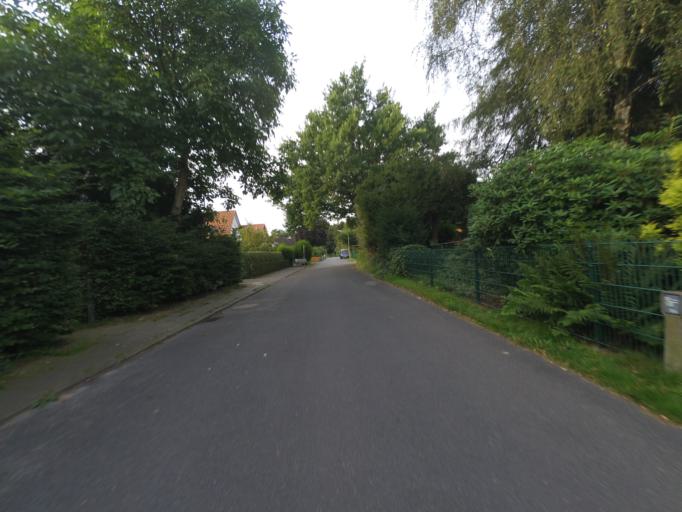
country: DE
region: Hamburg
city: Wandsbek
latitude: 53.5543
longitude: 10.1183
